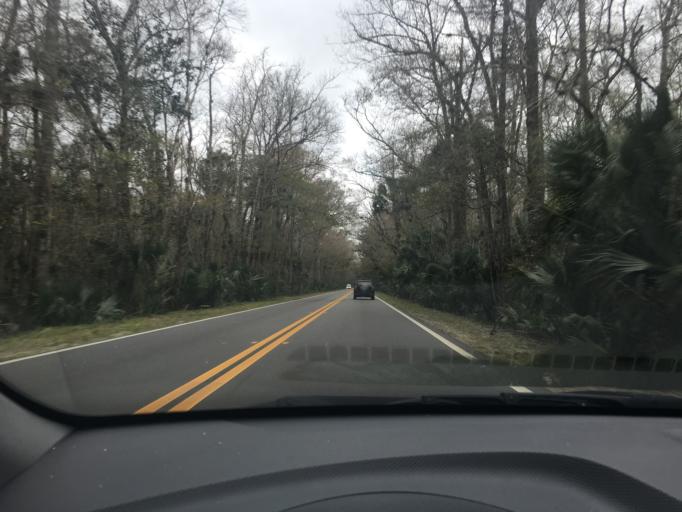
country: US
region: Florida
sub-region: Saint Johns County
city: Villano Beach
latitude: 29.9945
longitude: -81.4273
